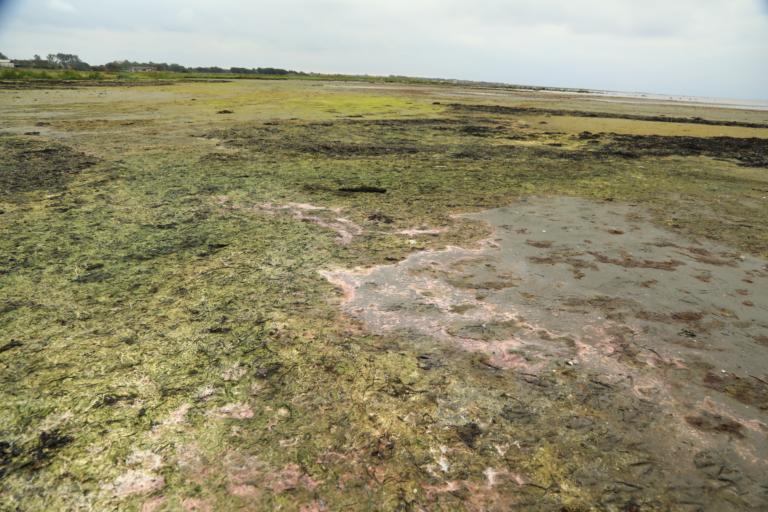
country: SE
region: Halland
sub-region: Varbergs Kommun
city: Tvaaker
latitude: 56.9899
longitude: 12.3557
